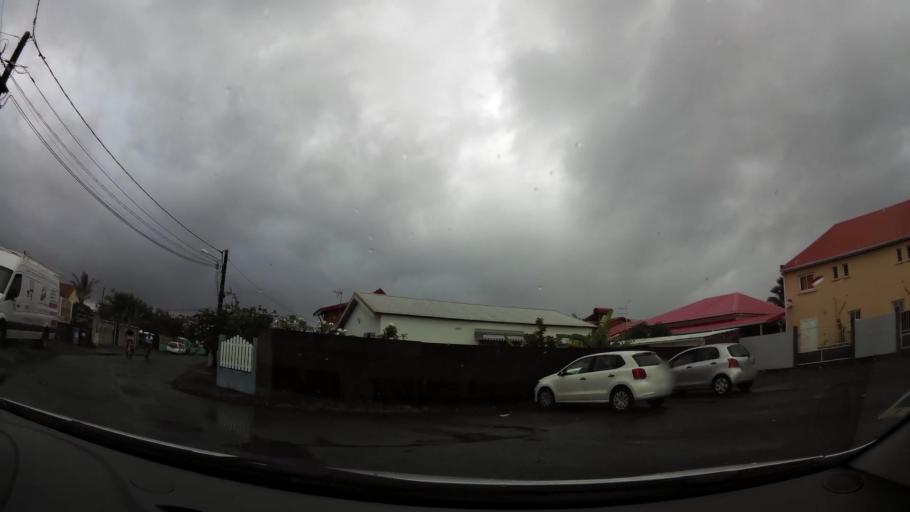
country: RE
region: Reunion
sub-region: Reunion
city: Saint-Andre
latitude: -20.9350
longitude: 55.6495
